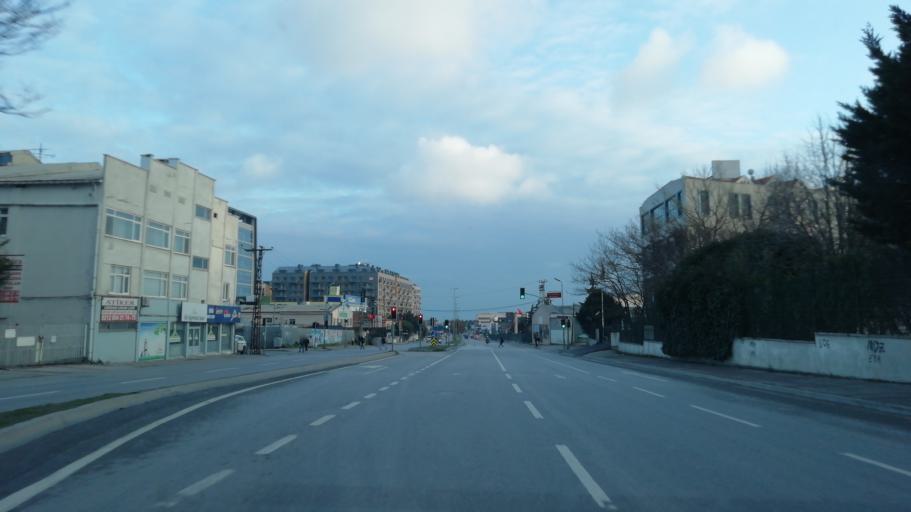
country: TR
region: Istanbul
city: Yakuplu
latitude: 40.9951
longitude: 28.7155
